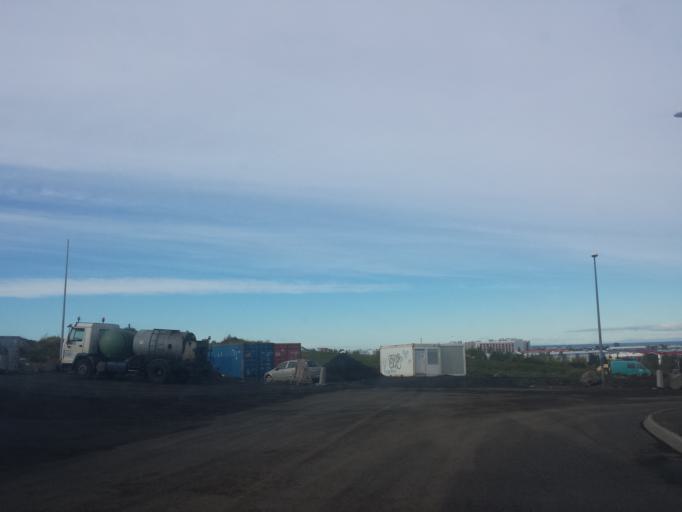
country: IS
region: Capital Region
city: Reykjavik
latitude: 64.0965
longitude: -21.8125
